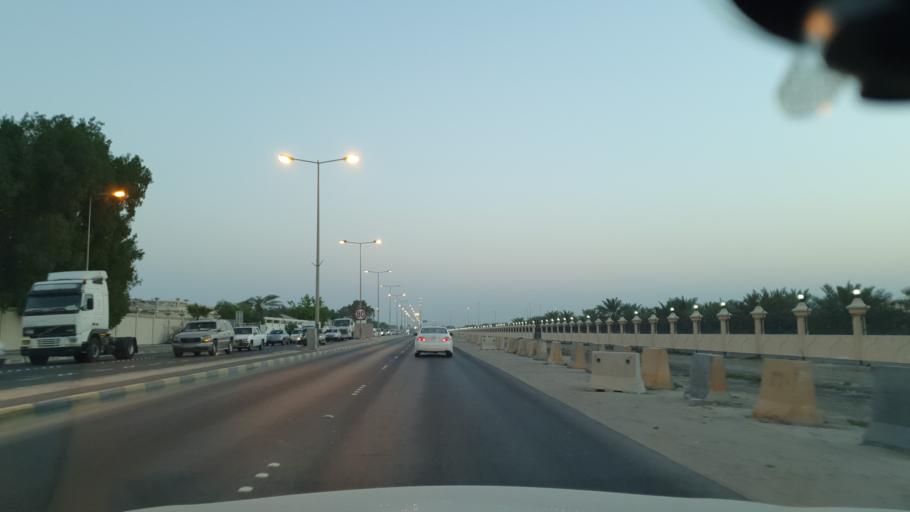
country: BH
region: Central Governorate
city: Madinat Hamad
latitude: 26.1818
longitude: 50.4657
